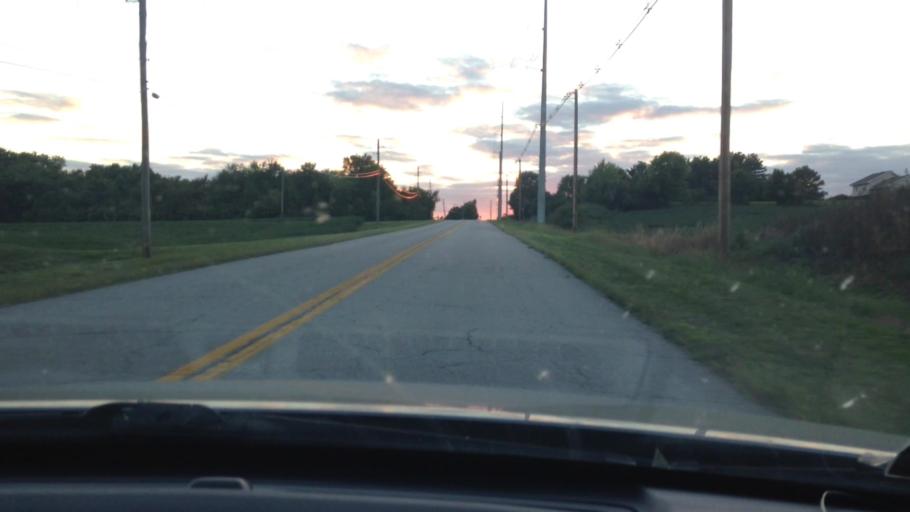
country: US
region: Kansas
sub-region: Leavenworth County
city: Lansing
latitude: 39.1867
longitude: -94.8198
